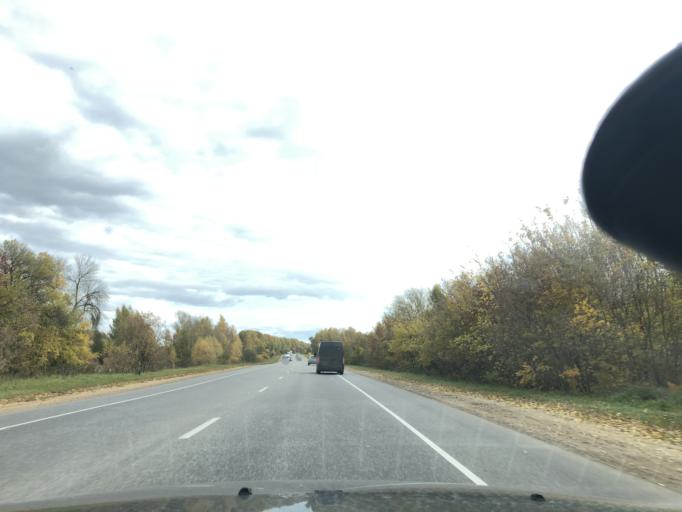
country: RU
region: Tula
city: Bolokhovo
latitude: 54.0774
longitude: 37.7854
